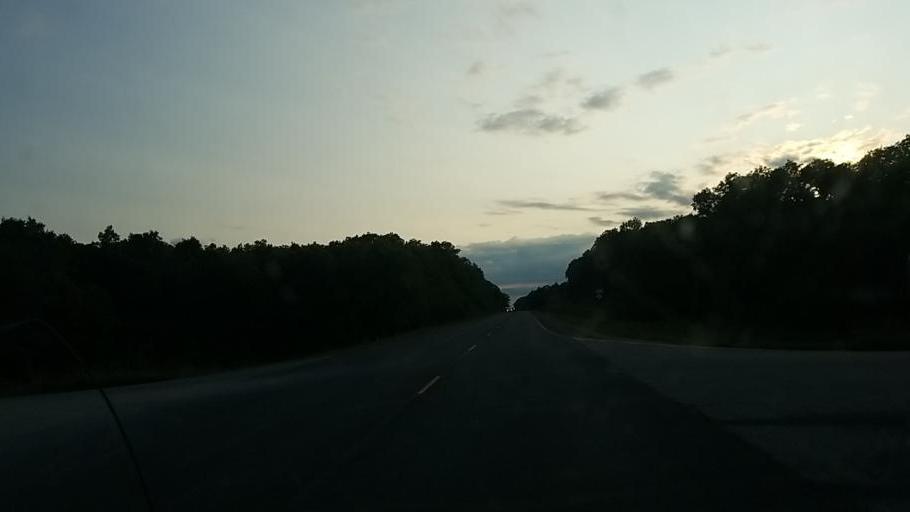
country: US
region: Michigan
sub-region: Newaygo County
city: Newaygo
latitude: 43.4055
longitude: -85.7121
